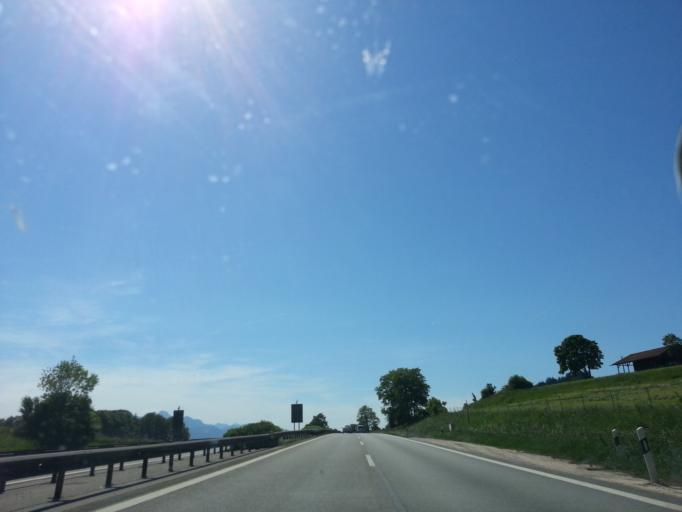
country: DE
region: Bavaria
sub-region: Upper Bavaria
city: Bergen
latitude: 47.8281
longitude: 12.5798
